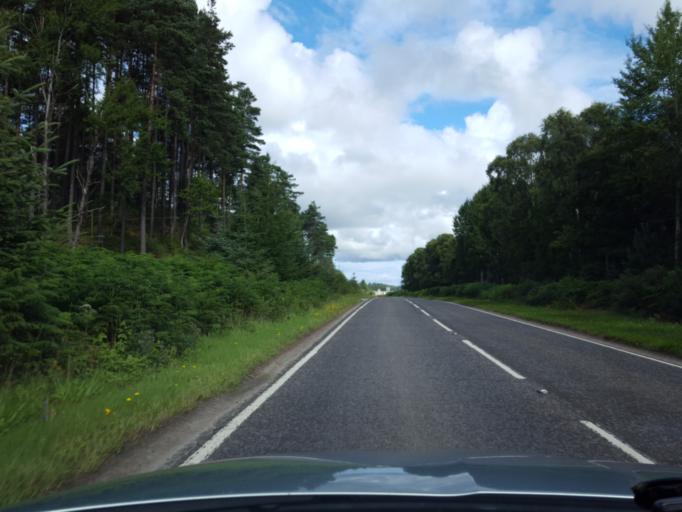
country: GB
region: Scotland
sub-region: Moray
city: Rothes
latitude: 57.5645
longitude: -3.2520
